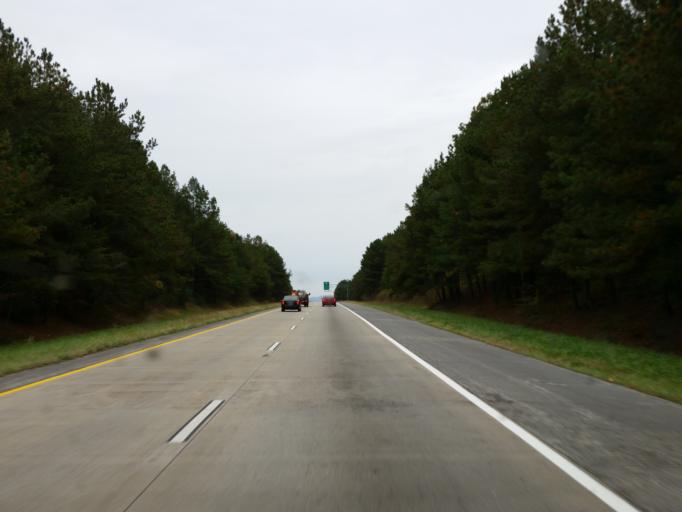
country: US
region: Georgia
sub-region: Cherokee County
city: Ball Ground
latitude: 34.3600
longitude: -84.3902
